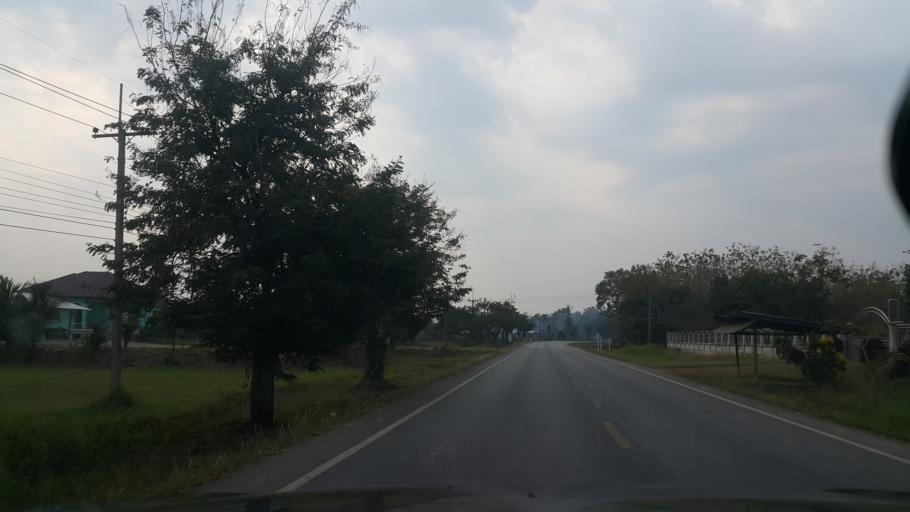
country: TH
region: Sukhothai
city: Si Samrong
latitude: 17.1091
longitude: 99.8892
